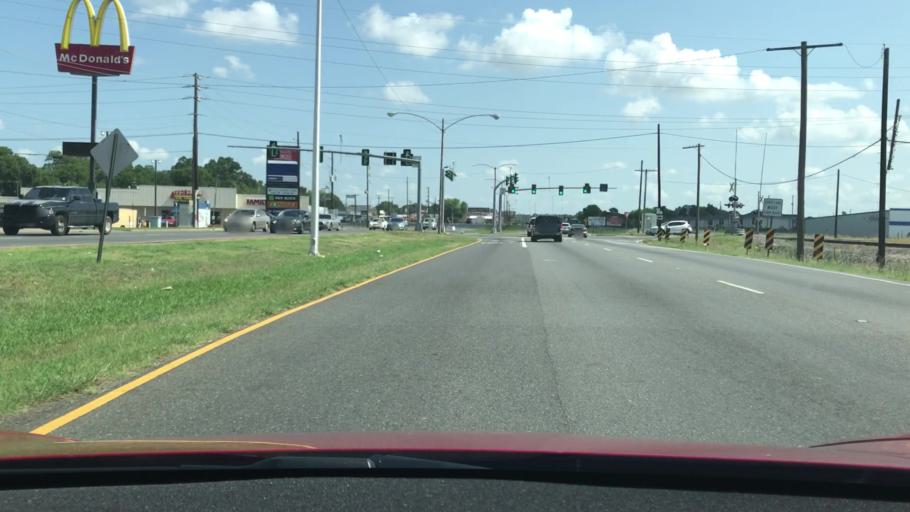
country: US
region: Louisiana
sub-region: Bossier Parish
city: Bossier City
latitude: 32.4412
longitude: -93.7813
